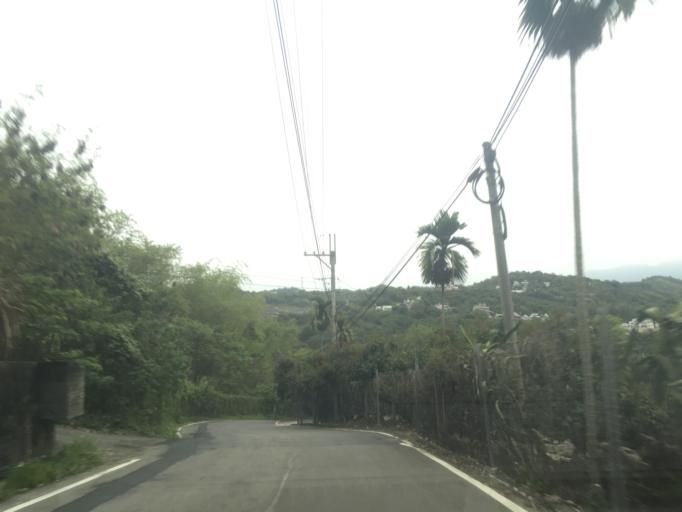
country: TW
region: Taiwan
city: Zhongxing New Village
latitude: 24.0327
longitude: 120.7228
